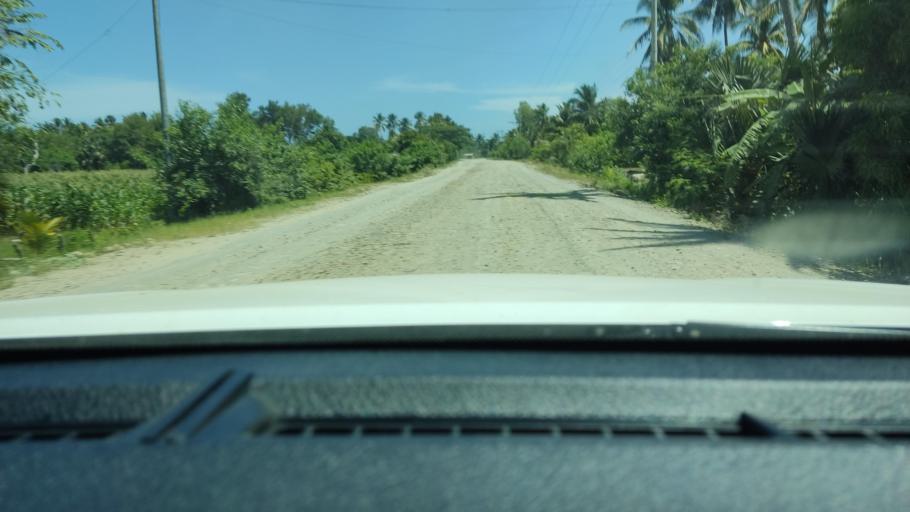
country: SV
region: Ahuachapan
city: San Francisco Menendez
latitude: 13.7663
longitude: -90.1155
